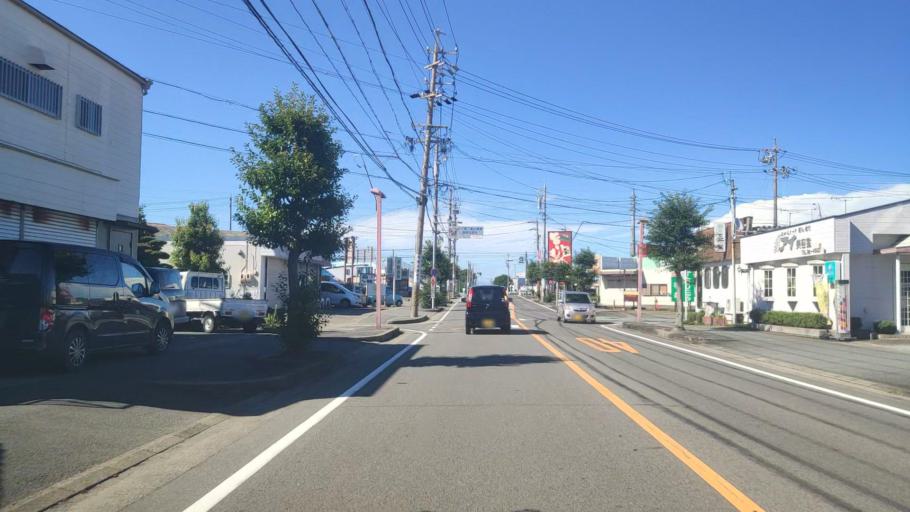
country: JP
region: Mie
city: Ise
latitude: 34.5057
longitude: 136.7086
